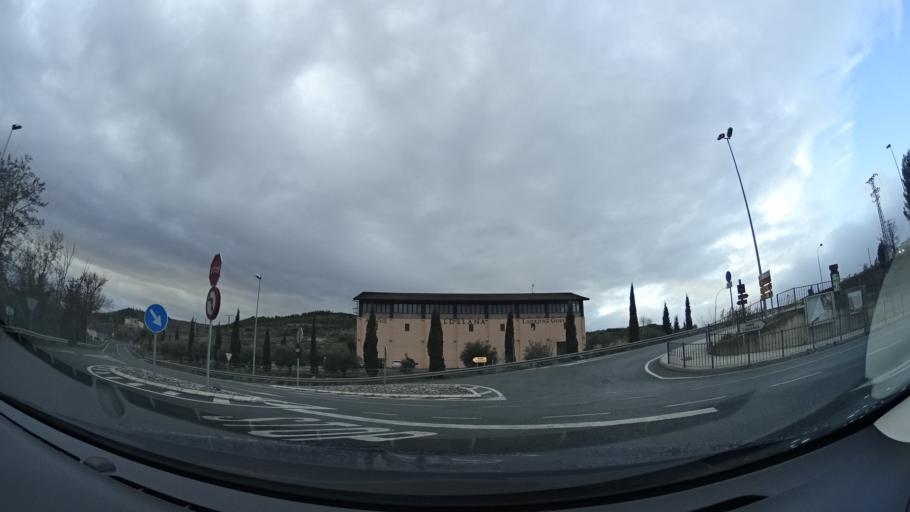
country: ES
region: Basque Country
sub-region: Provincia de Alava
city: Elciego
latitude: 42.5109
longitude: -2.6206
